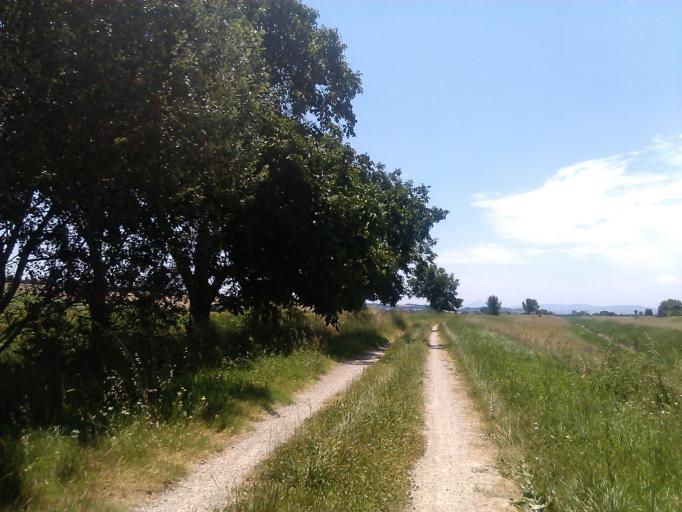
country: IT
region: Tuscany
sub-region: Province of Arezzo
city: Cesa
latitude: 43.2935
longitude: 11.8415
